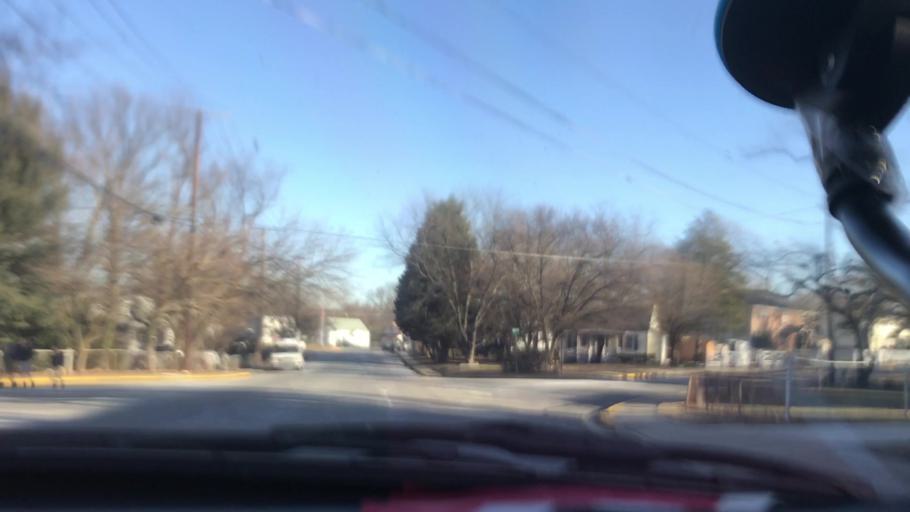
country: US
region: Maryland
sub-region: Prince George's County
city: Morningside
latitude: 38.8288
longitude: -76.8935
